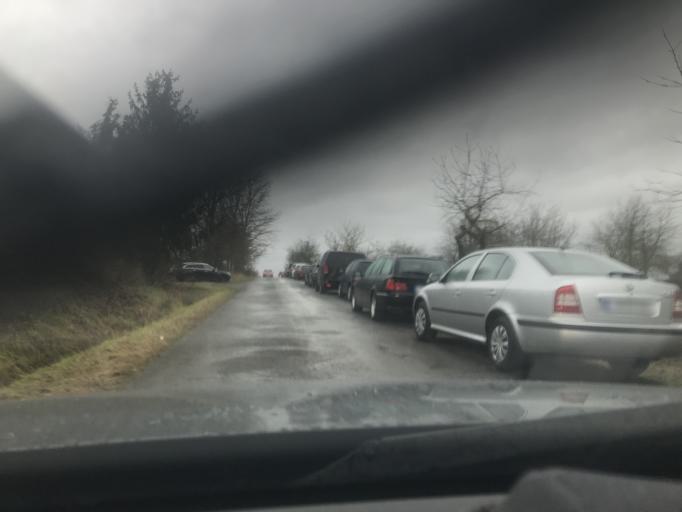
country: DE
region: Thuringia
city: Muehlhausen
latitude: 51.2253
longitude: 10.4198
